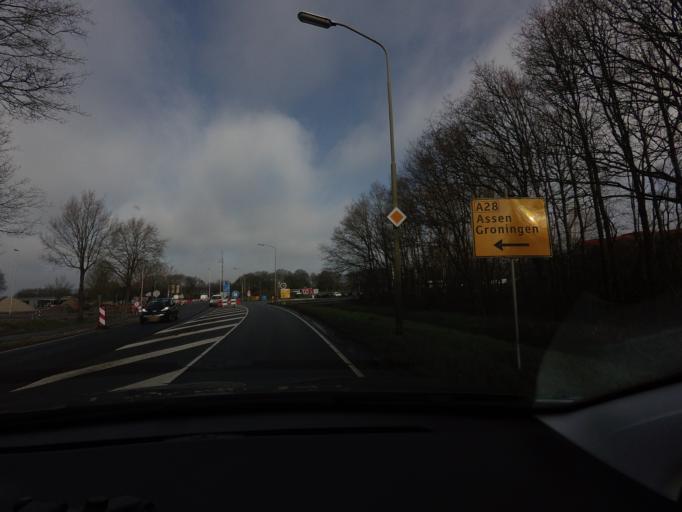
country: NL
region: Drenthe
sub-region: Gemeente Westerveld
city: Dwingeloo
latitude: 52.8572
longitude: 6.5000
